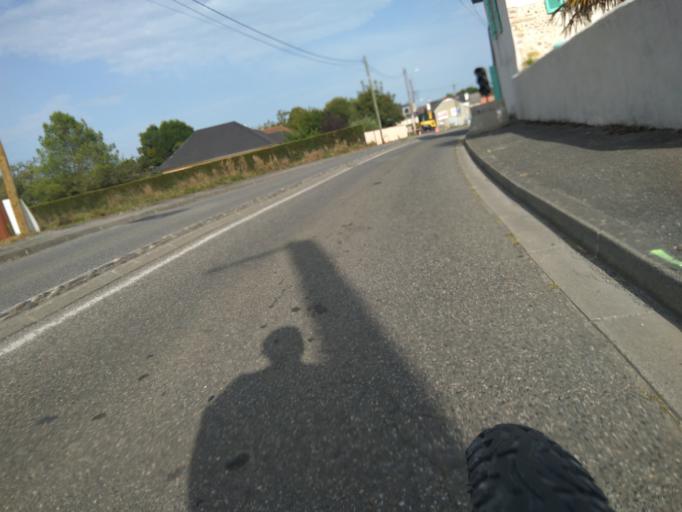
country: FR
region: Aquitaine
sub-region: Departement des Pyrenees-Atlantiques
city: Mazeres-Lezons
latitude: 43.2748
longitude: -0.3491
